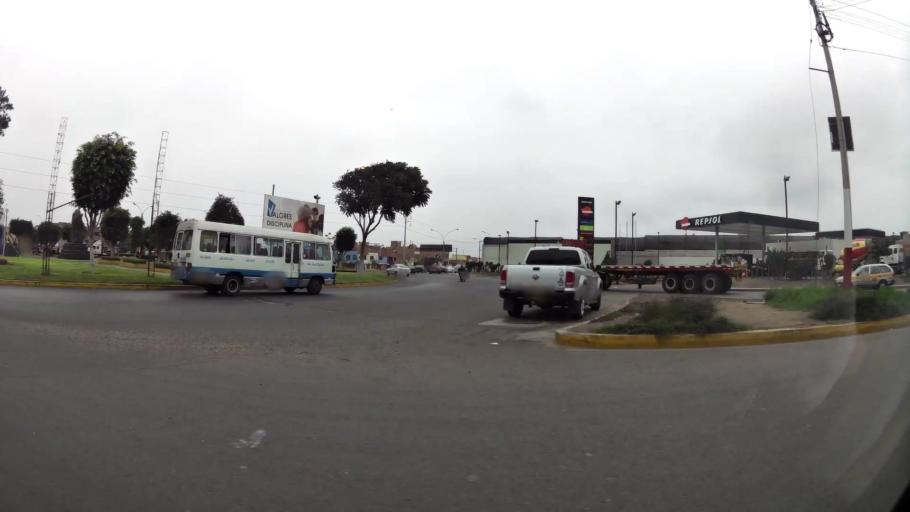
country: PE
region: Callao
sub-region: Callao
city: Callao
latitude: -12.0504
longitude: -77.1258
